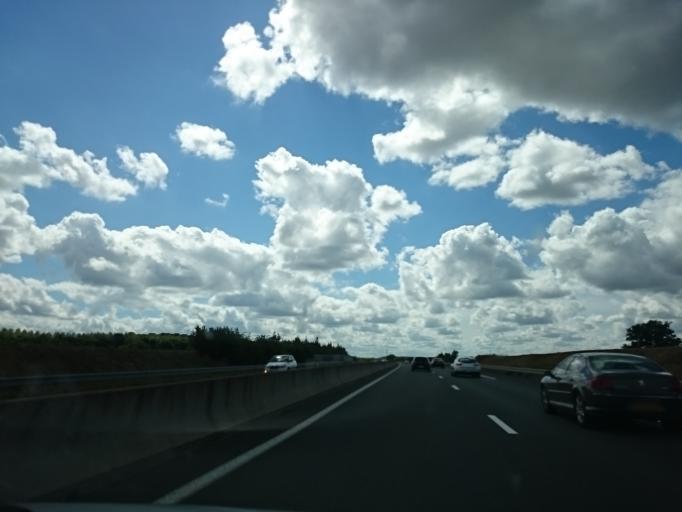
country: FR
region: Pays de la Loire
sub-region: Departement de Maine-et-Loire
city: Saint-Lambert-la-Potherie
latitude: 47.4876
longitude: -0.6565
